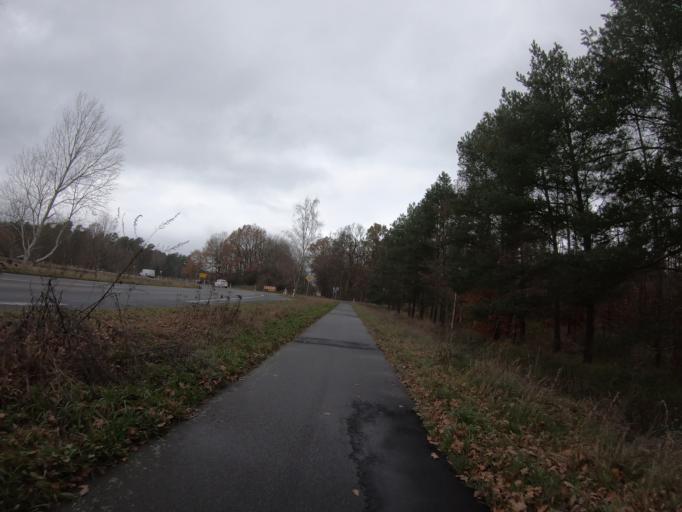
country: DE
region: Lower Saxony
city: Wagenhoff
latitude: 52.5493
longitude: 10.5150
